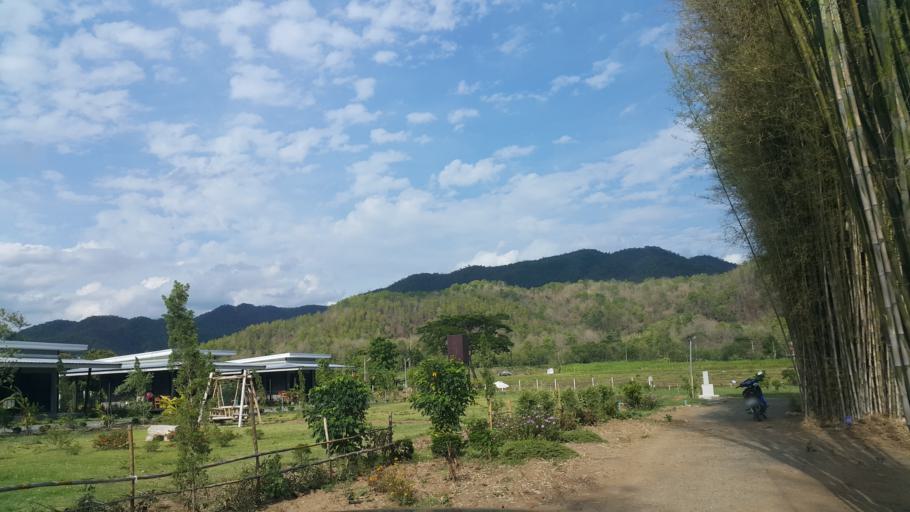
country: TH
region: Chiang Mai
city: Mae On
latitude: 18.7914
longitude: 99.2600
